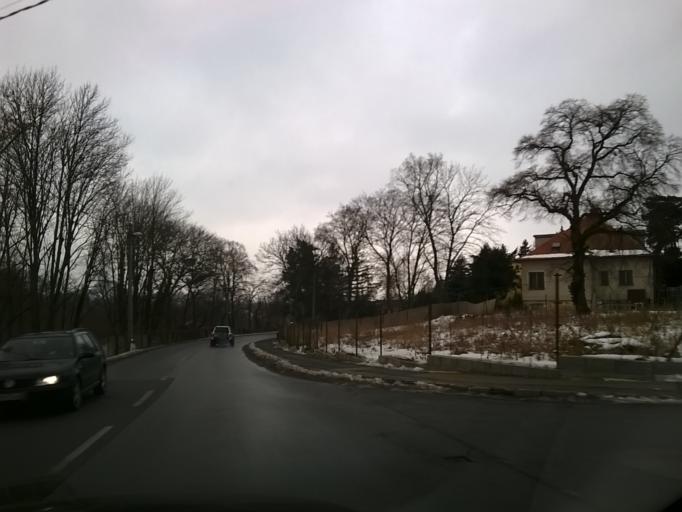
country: SK
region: Nitriansky
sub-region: Okres Nitra
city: Nitra
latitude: 48.3235
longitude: 18.1025
